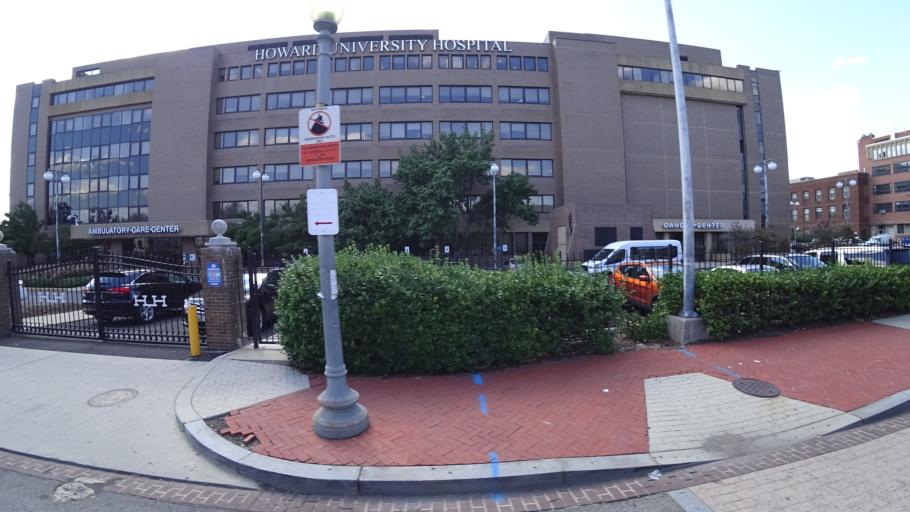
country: US
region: Washington, D.C.
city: Washington, D.C.
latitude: 38.9178
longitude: -77.0189
